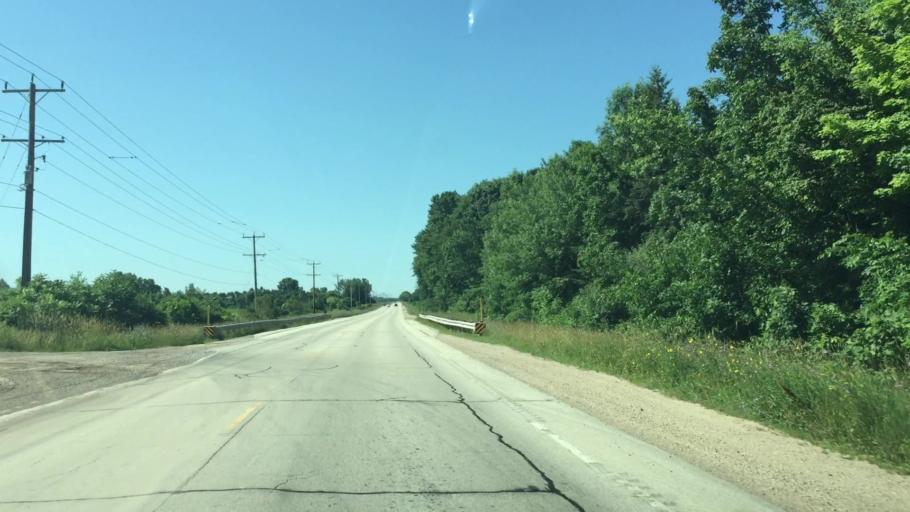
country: US
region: Wisconsin
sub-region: Calumet County
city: Sherwood
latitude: 44.1558
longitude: -88.2648
